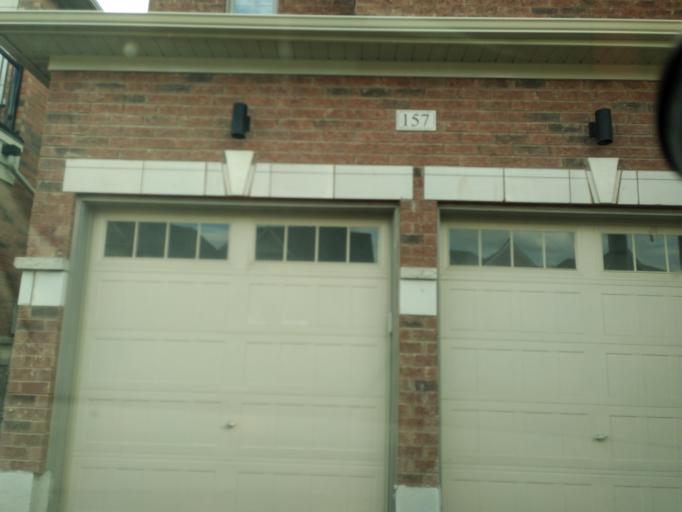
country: CA
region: Ontario
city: Newmarket
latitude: 44.0972
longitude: -79.5064
